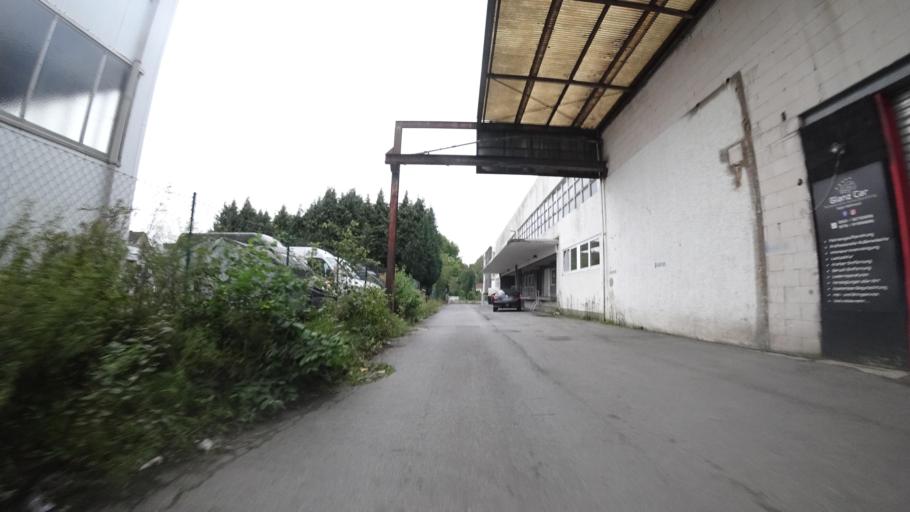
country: DE
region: North Rhine-Westphalia
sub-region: Regierungsbezirk Detmold
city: Bielefeld
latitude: 52.0393
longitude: 8.5522
